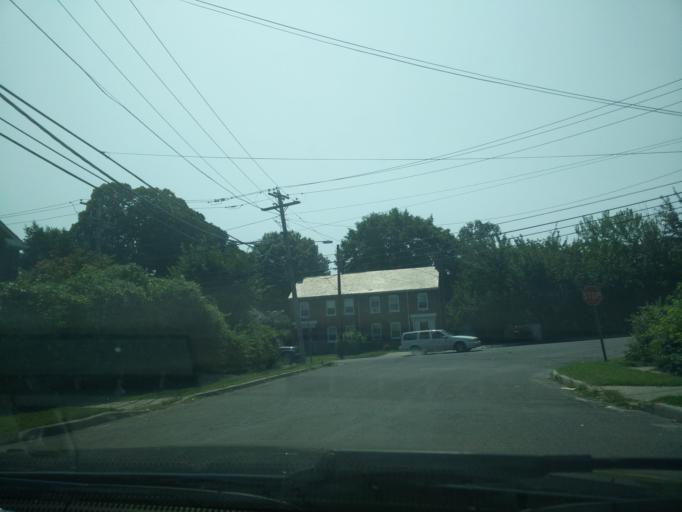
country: US
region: Connecticut
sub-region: Fairfield County
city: Fairfield
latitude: 41.1556
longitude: -73.2404
